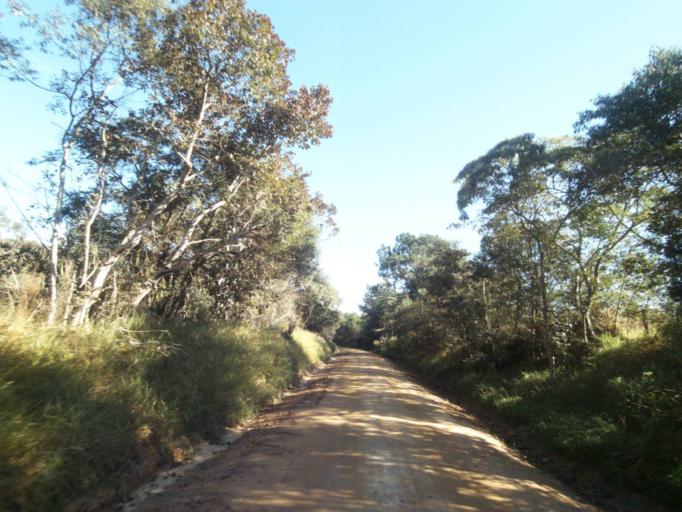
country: BR
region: Parana
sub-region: Tibagi
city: Tibagi
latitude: -24.5344
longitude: -50.3746
